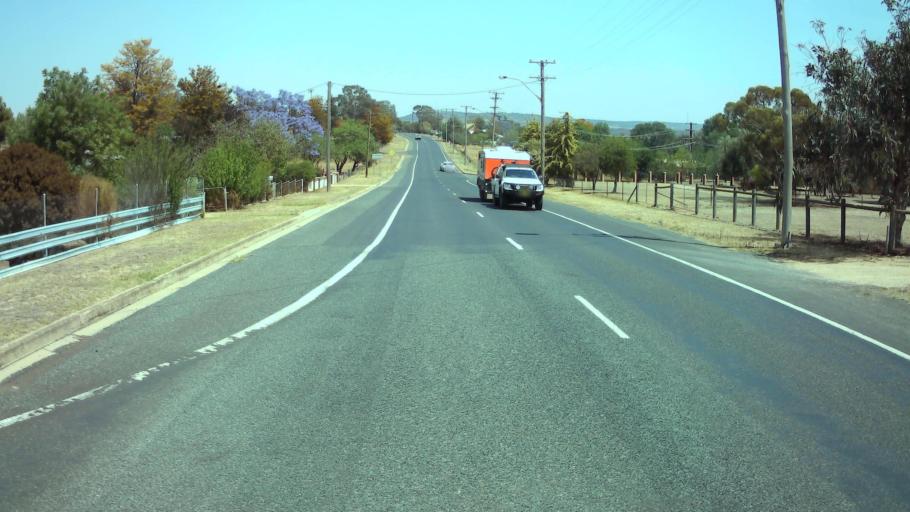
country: AU
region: New South Wales
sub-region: Weddin
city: Grenfell
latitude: -33.8969
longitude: 148.1732
